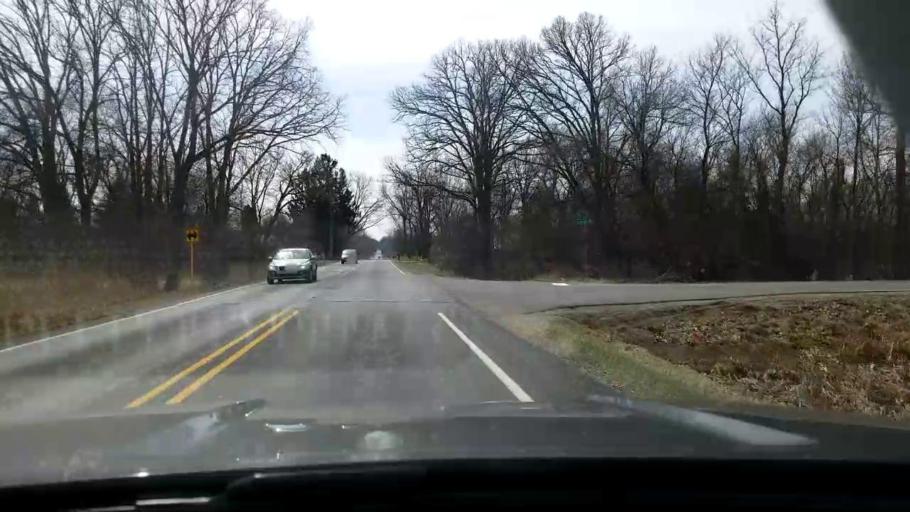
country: US
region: Michigan
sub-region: Jackson County
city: Spring Arbor
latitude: 42.2002
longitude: -84.5210
